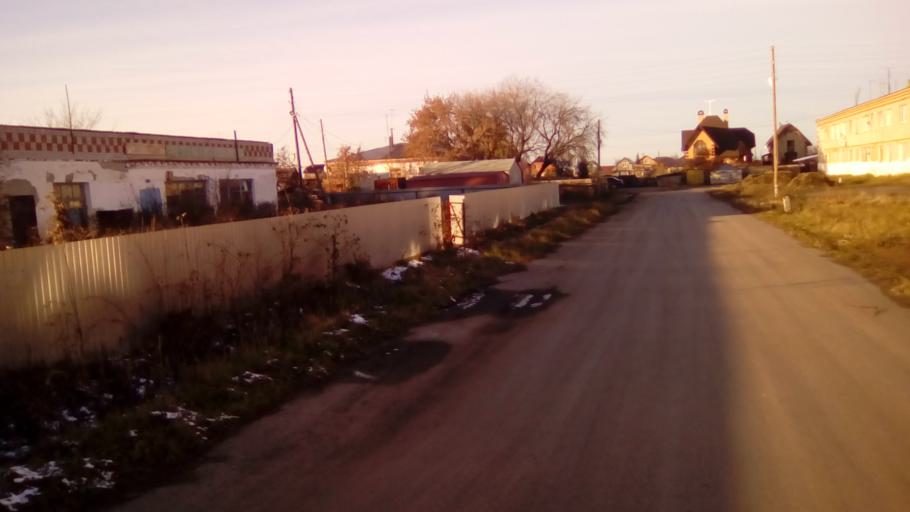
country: RU
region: Tjumen
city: Moskovskiy
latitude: 57.2207
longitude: 65.3552
